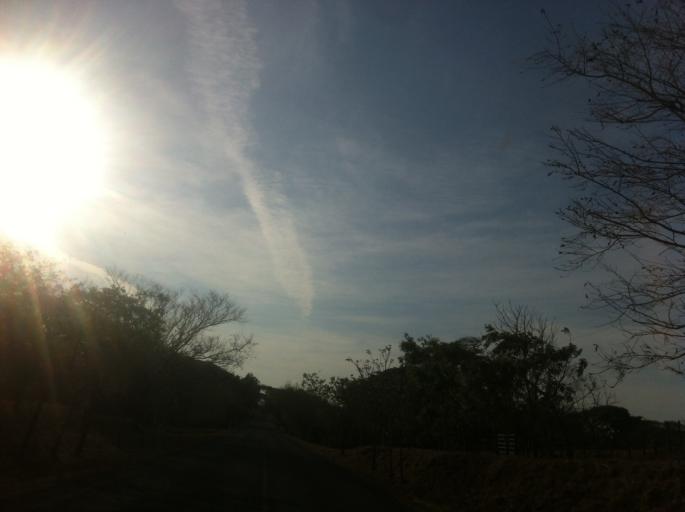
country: NI
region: Rivas
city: Cardenas
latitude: 11.2800
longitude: -85.6679
